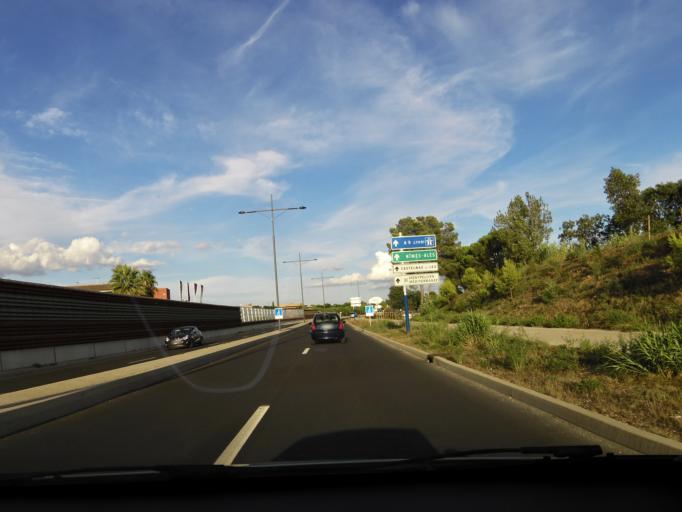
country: FR
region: Languedoc-Roussillon
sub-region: Departement de l'Herault
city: Clapiers
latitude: 43.6548
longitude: 3.8770
